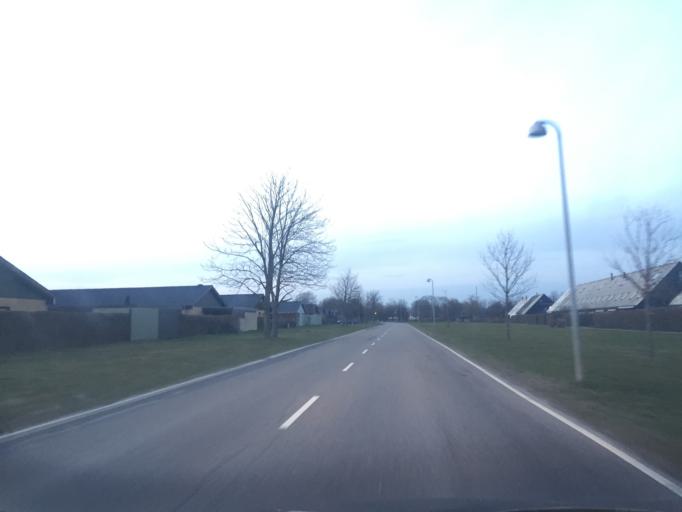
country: DK
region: Capital Region
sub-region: Hoje-Taastrup Kommune
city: Taastrup
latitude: 55.6395
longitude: 12.3088
